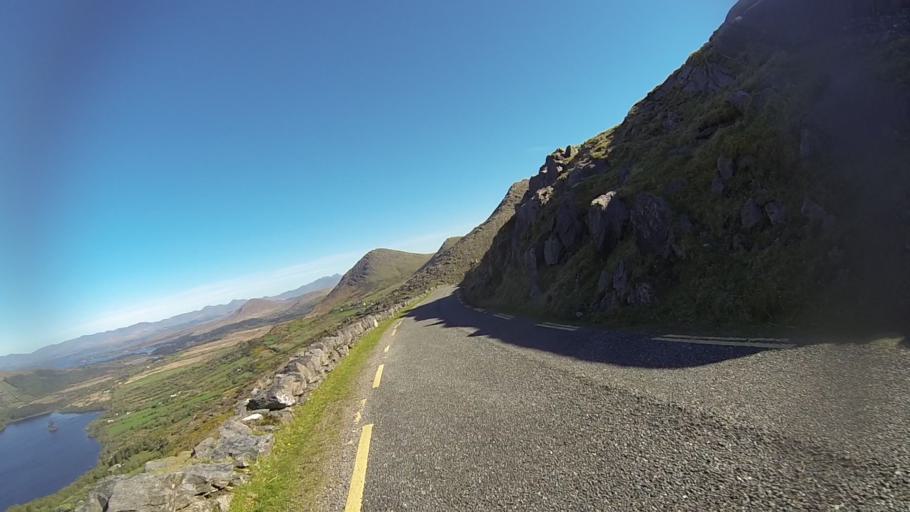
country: IE
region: Munster
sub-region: Ciarrai
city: Kenmare
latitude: 51.7257
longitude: -9.7583
